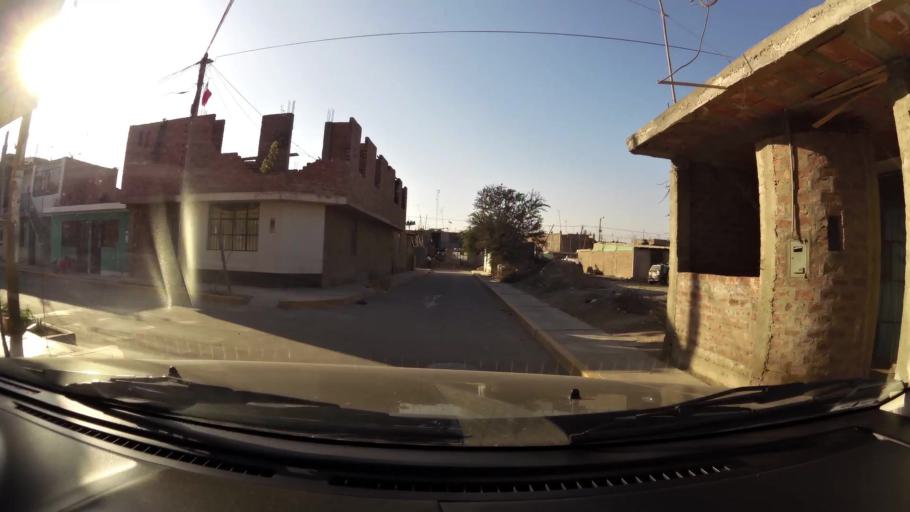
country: PE
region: Ica
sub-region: Provincia de Ica
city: Ica
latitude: -14.0647
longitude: -75.7182
